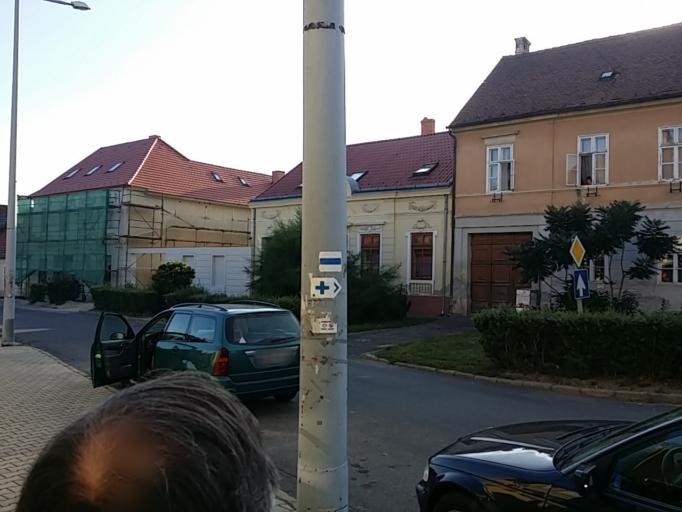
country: HU
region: Vas
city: Koszeg
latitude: 47.3920
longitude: 16.5390
